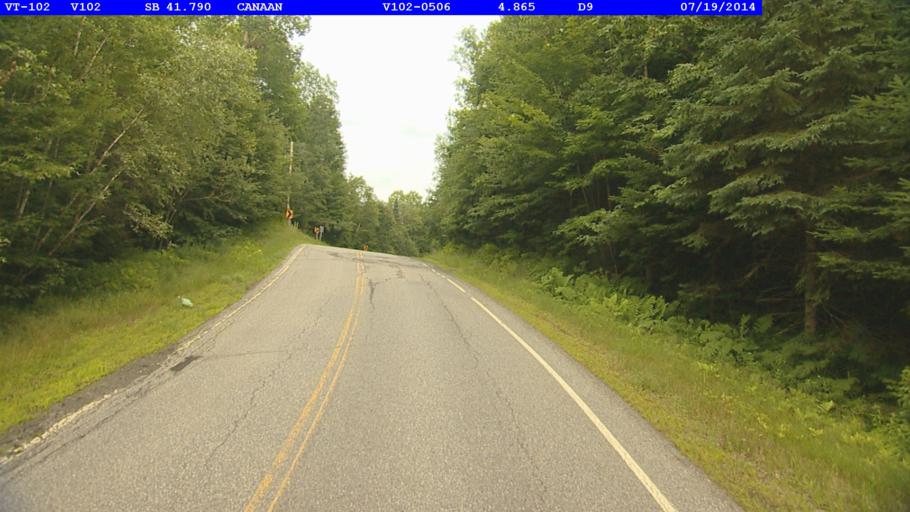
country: US
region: New Hampshire
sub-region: Coos County
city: Colebrook
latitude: 44.9721
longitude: -71.5319
